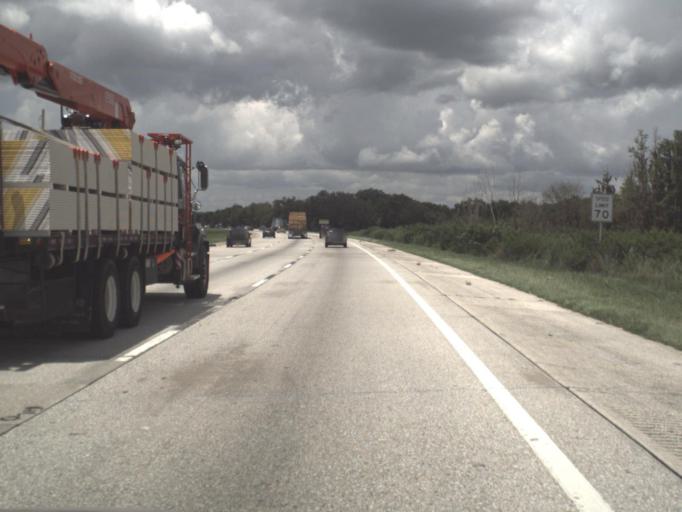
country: US
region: Florida
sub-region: Hillsborough County
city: Mango
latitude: 28.0154
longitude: -82.3293
